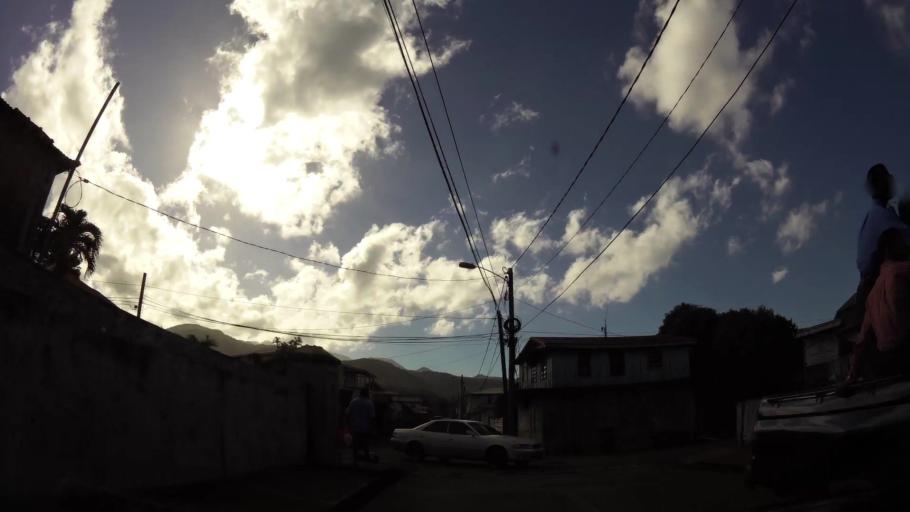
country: DM
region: Saint John
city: Portsmouth
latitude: 15.5775
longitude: -61.4563
